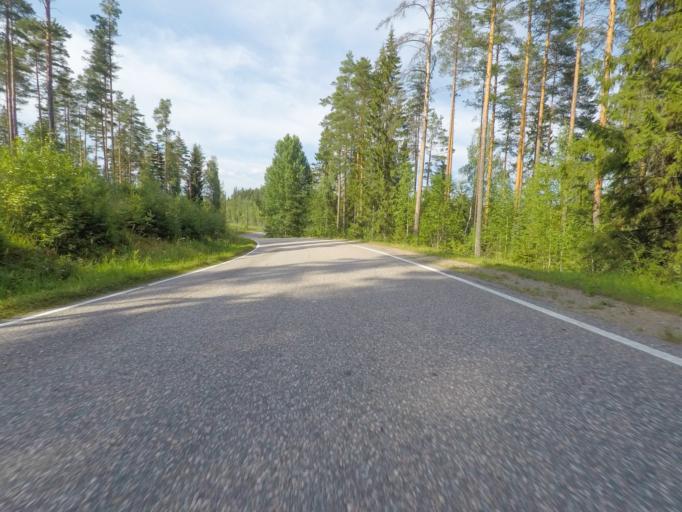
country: FI
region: Southern Savonia
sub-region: Savonlinna
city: Sulkava
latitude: 61.7811
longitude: 28.2398
